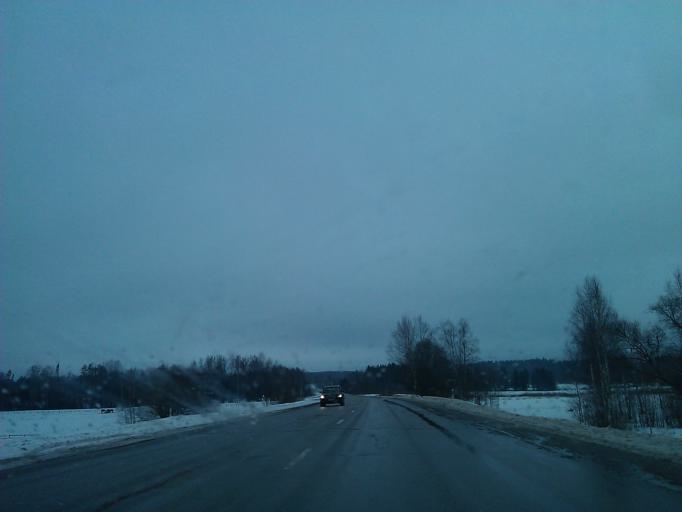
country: LV
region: Cesu Rajons
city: Cesis
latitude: 57.2849
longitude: 25.2956
